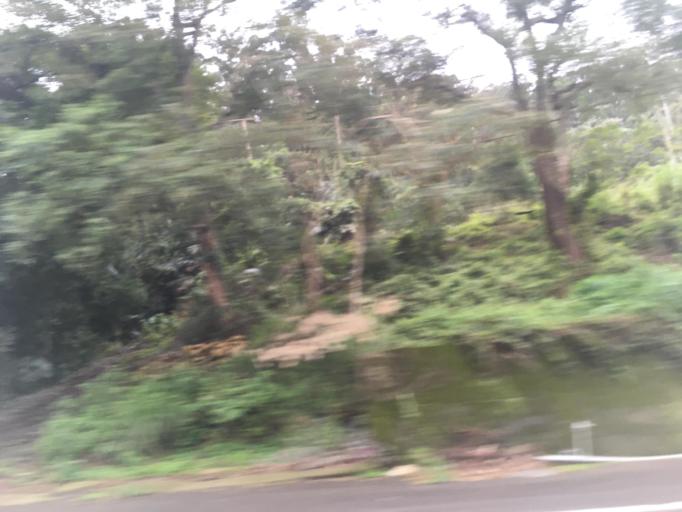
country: TW
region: Taiwan
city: Fengyuan
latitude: 24.4115
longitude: 120.7404
